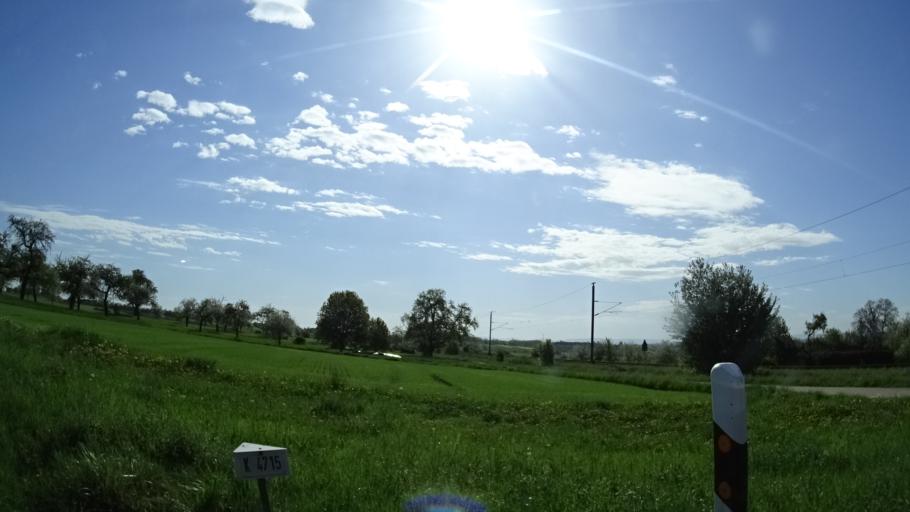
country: DE
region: Baden-Wuerttemberg
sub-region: Regierungsbezirk Stuttgart
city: Motzingen
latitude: 48.4849
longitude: 8.7546
